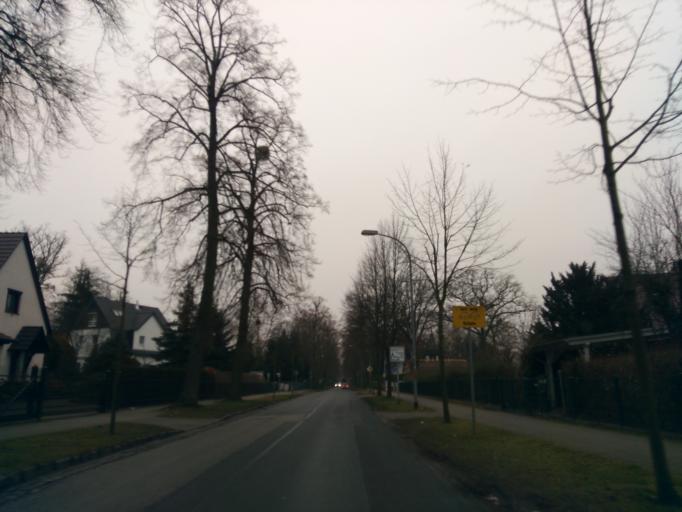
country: DE
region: Brandenburg
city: Dallgow-Doeberitz
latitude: 52.5554
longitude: 13.0528
